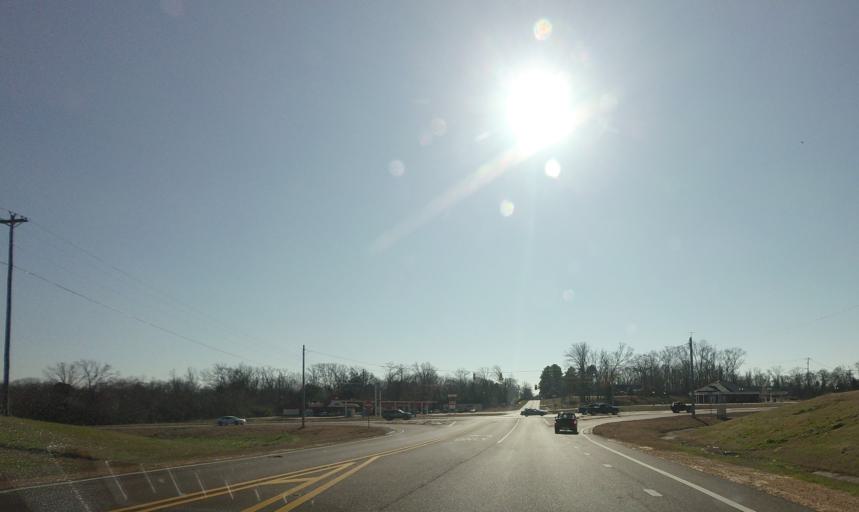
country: US
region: Tennessee
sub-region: Shelby County
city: Collierville
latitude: 34.9637
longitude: -89.6890
